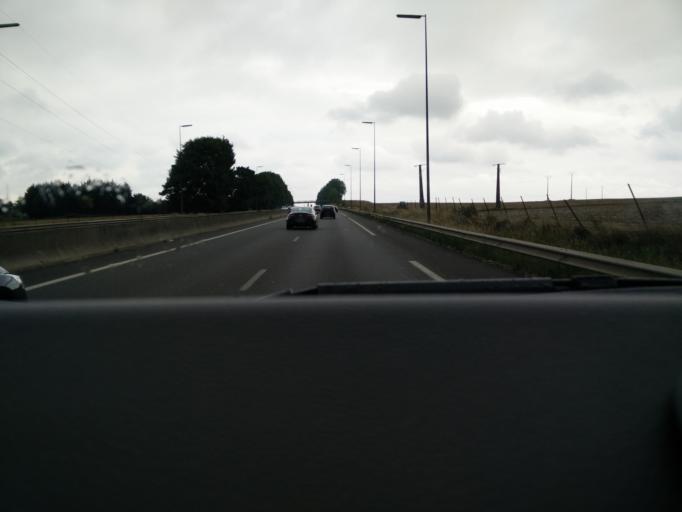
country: FR
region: Nord-Pas-de-Calais
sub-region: Departement du Pas-de-Calais
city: Bully-les-Mines
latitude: 50.4350
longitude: 2.7230
